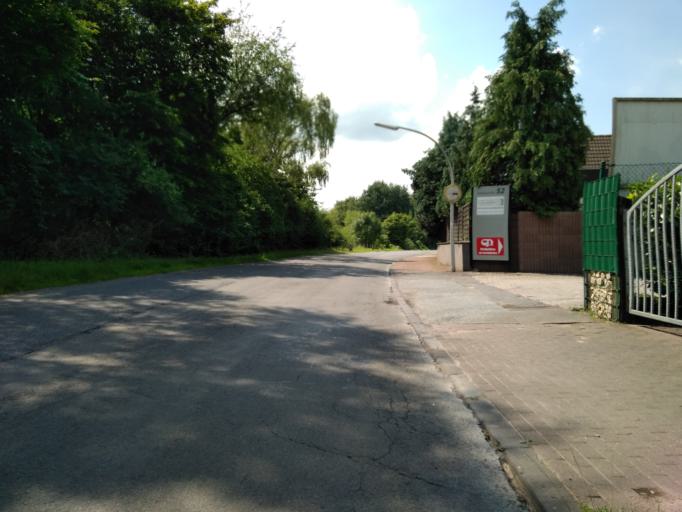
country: DE
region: North Rhine-Westphalia
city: Dorsten
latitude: 51.6716
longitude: 6.9561
